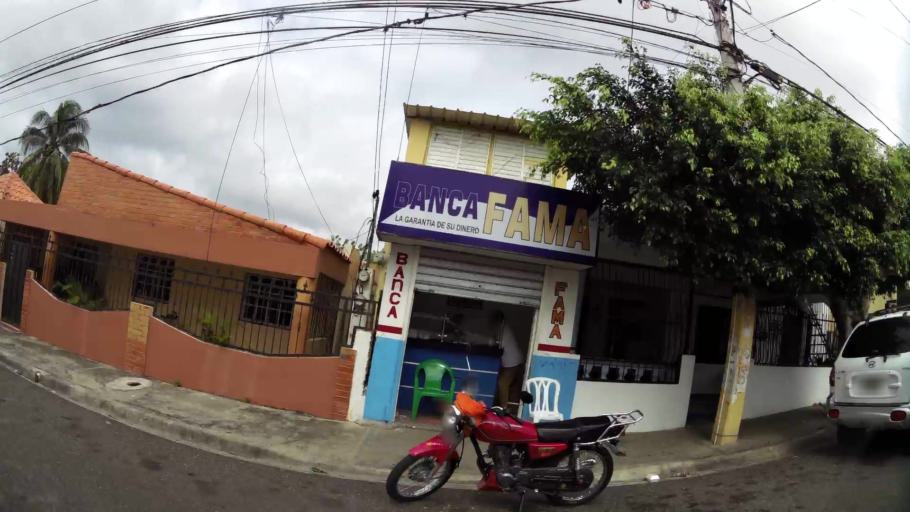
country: DO
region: Santiago
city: Santiago de los Caballeros
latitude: 19.4656
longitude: -70.6736
